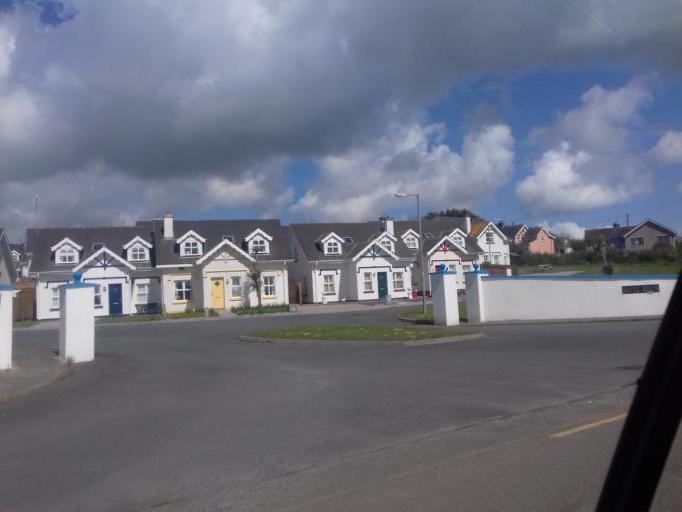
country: IE
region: Munster
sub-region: Waterford
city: Dunmore East
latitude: 52.2198
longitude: -6.9225
